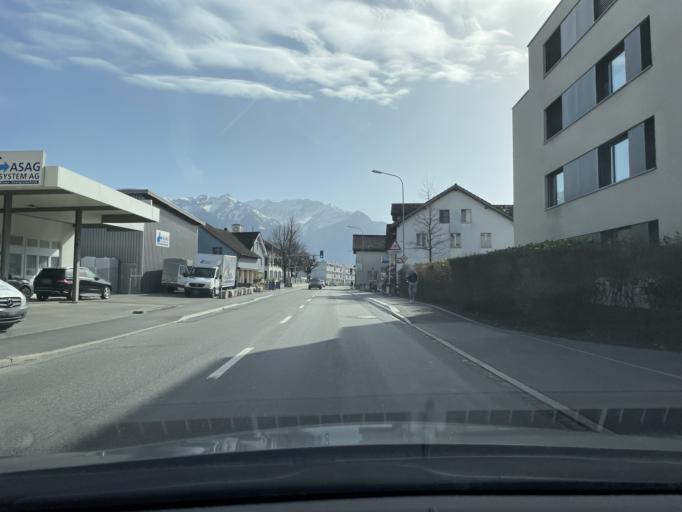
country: CH
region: Saint Gallen
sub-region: Wahlkreis Werdenberg
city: Buchs
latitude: 47.1498
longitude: 9.4828
